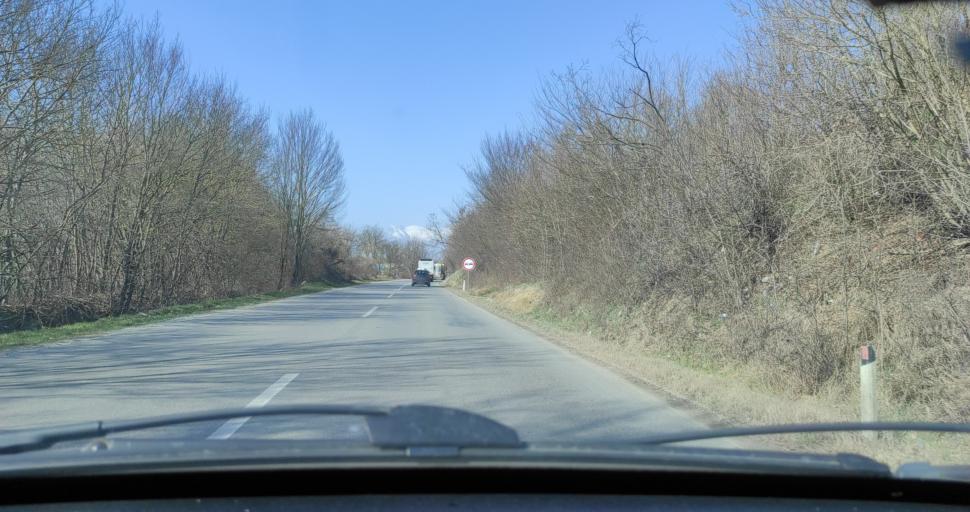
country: XK
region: Pec
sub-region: Komuna e Pejes
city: Kosuriq
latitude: 42.6292
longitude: 20.4549
